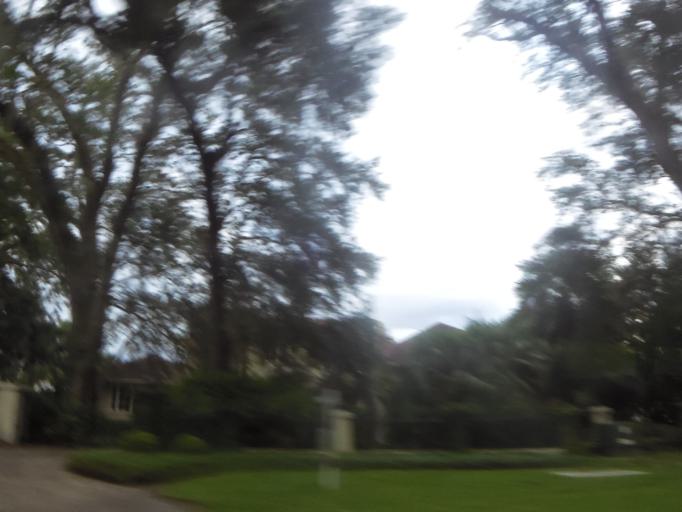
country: US
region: Florida
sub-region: Duval County
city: Jacksonville
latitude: 30.2672
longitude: -81.7012
